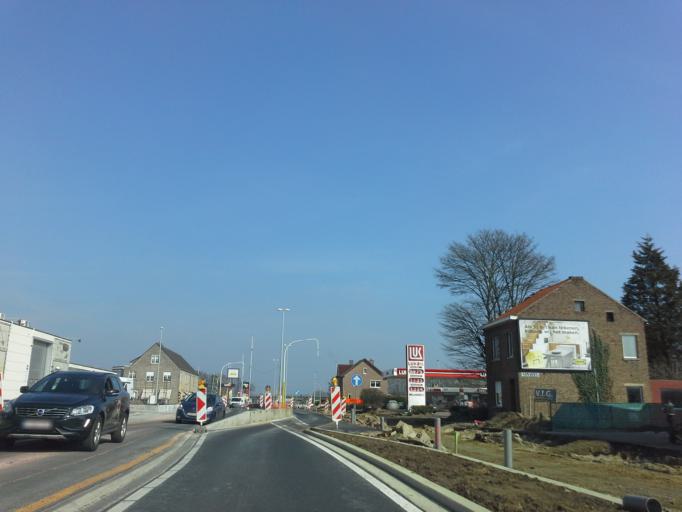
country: BE
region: Flanders
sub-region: Provincie Limburg
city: Hoeselt
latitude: 50.8556
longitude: 5.4968
